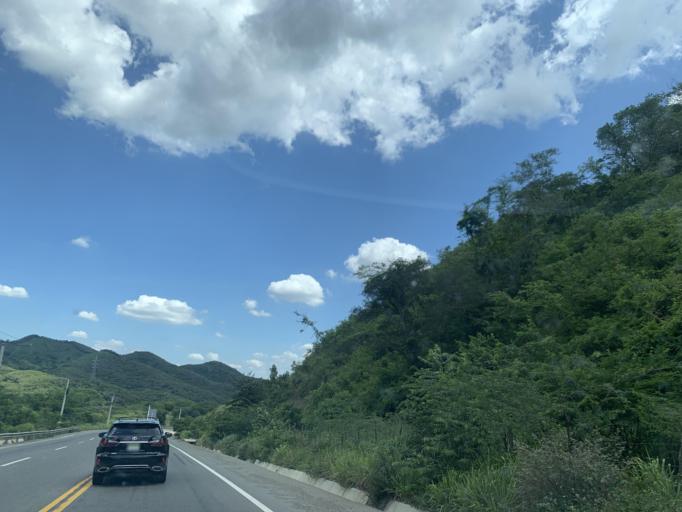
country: DO
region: Santiago
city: Villa Bisono
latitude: 19.6063
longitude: -70.8385
